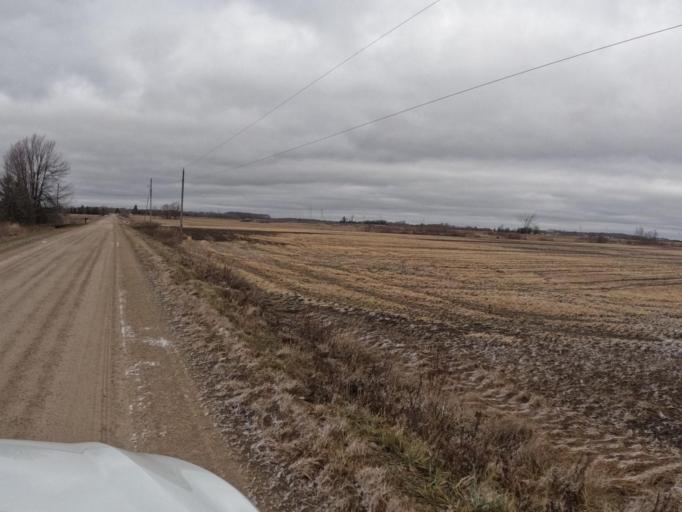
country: CA
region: Ontario
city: Shelburne
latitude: 44.0322
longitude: -80.3716
